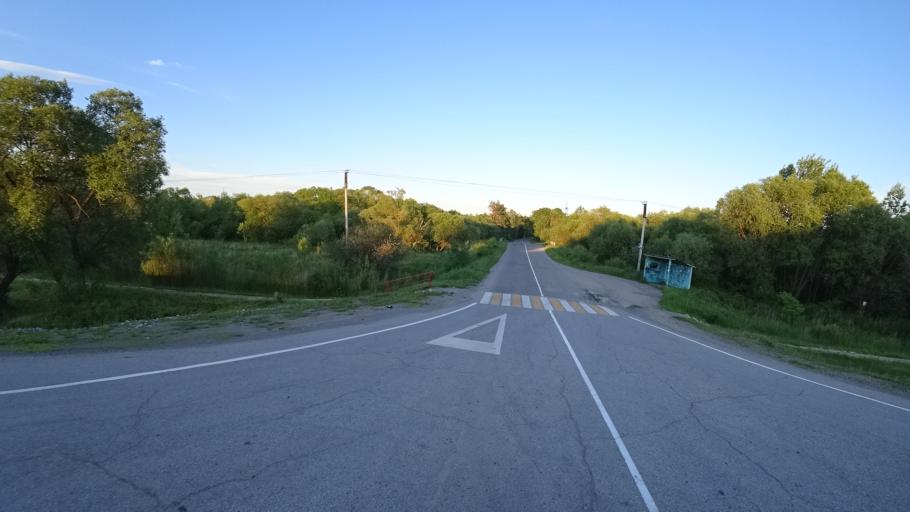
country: RU
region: Khabarovsk Krai
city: Khor
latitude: 47.8565
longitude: 134.9622
